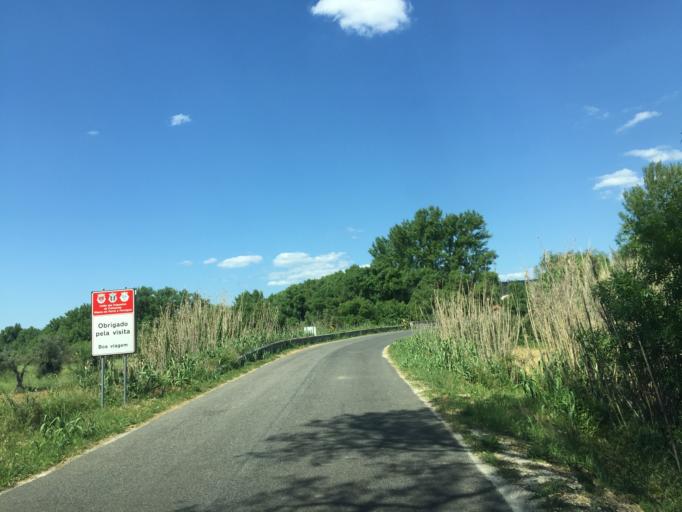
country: PT
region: Leiria
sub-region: Alvaiazere
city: Alvaiazere
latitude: 39.7768
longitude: -8.4629
